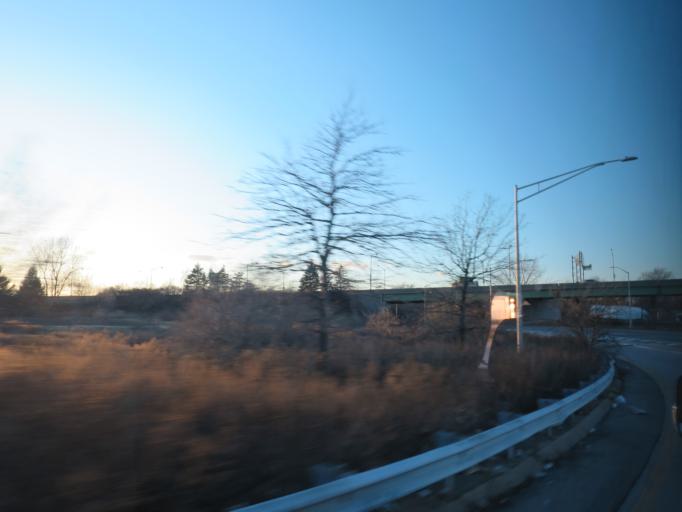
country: US
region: New York
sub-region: Queens County
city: Jamaica
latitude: 40.6651
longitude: -73.7876
